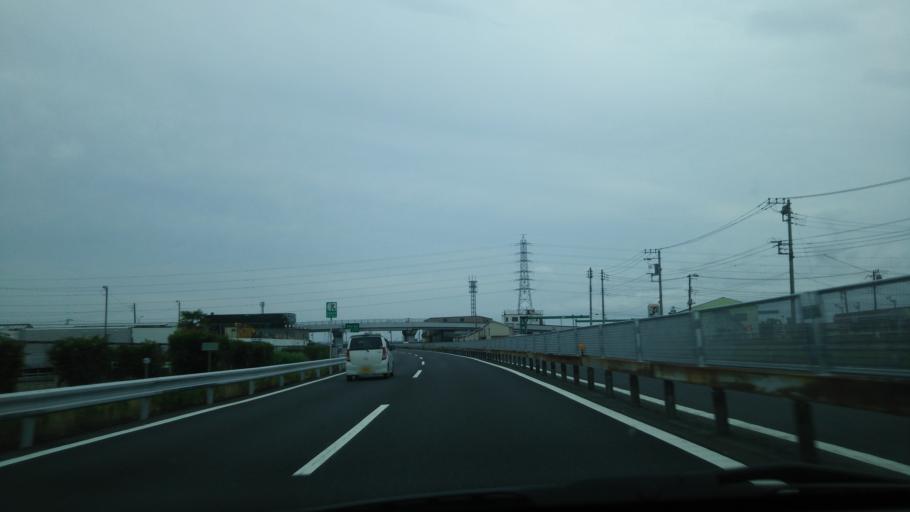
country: JP
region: Kanagawa
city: Isehara
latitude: 35.3754
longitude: 139.3239
